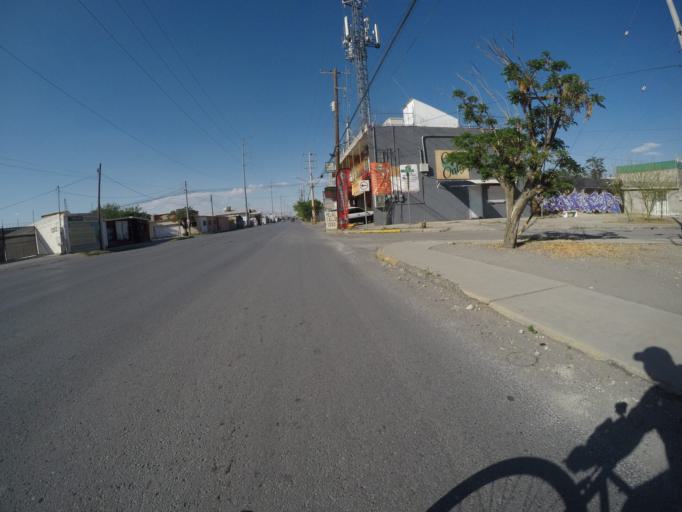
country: MX
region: Chihuahua
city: Ciudad Juarez
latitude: 31.7244
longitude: -106.4425
